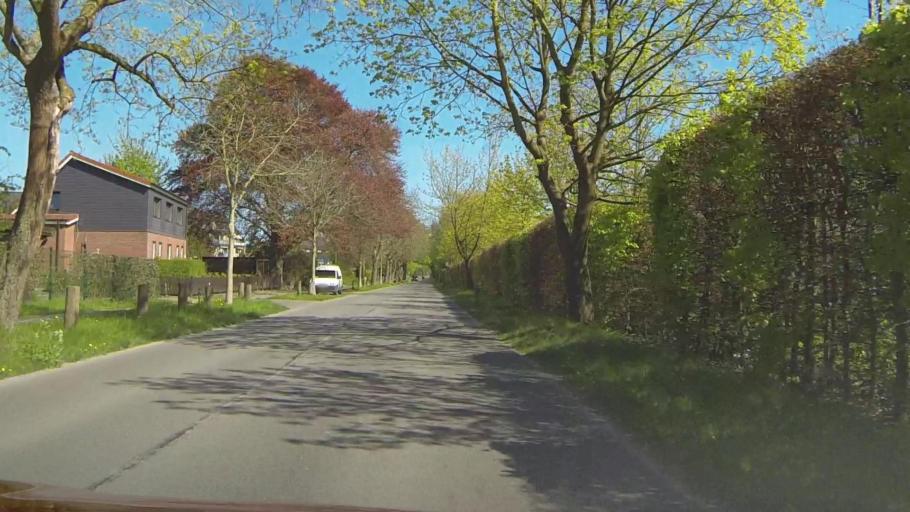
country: DE
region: Schleswig-Holstein
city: Uetersen
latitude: 53.6798
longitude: 9.6849
